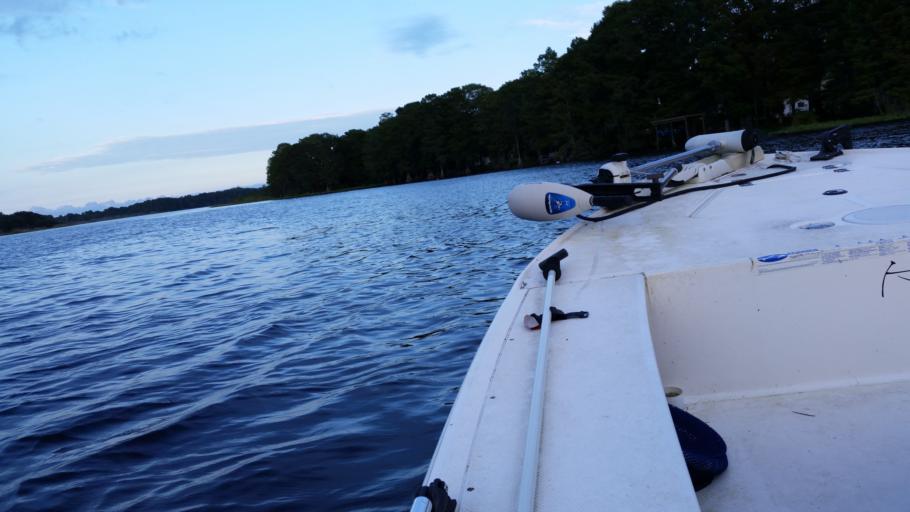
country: US
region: Florida
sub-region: Citrus County
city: Inverness
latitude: 28.8310
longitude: -82.3092
